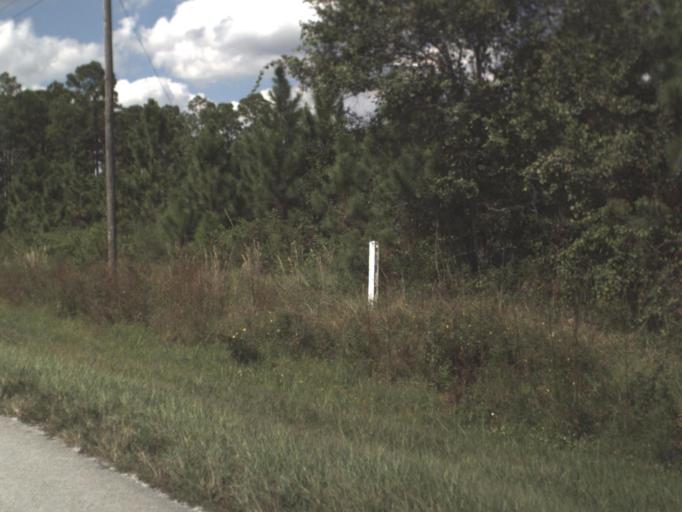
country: US
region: Florida
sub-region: Highlands County
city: Sebring
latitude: 27.4125
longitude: -81.4678
